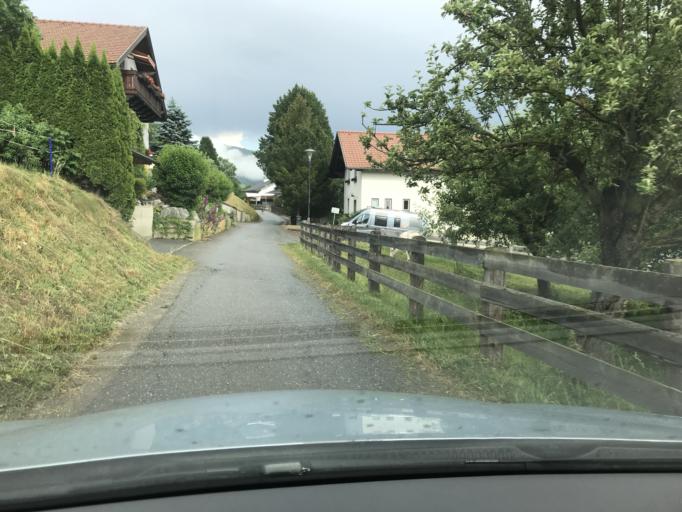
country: AT
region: Styria
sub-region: Politischer Bezirk Murau
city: Sankt Peter am Kammersberg
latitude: 47.1875
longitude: 14.1904
